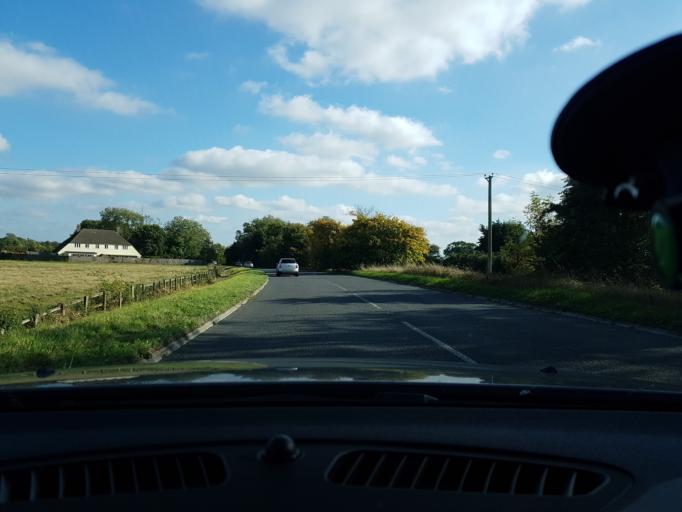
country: GB
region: England
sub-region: Wiltshire
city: Aldbourne
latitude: 51.4939
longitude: -1.5794
